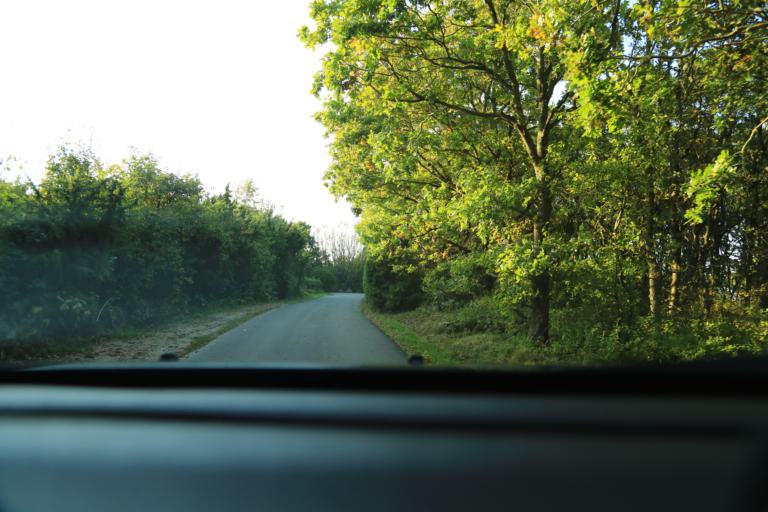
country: SE
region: Halland
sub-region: Varbergs Kommun
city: Traslovslage
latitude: 57.0404
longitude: 12.2953
